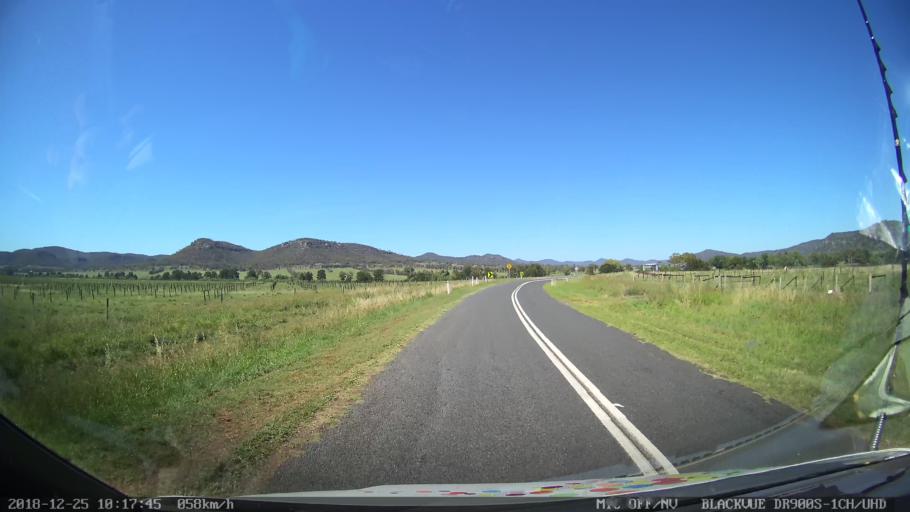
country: AU
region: New South Wales
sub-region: Muswellbrook
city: Denman
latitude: -32.3446
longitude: 150.5767
